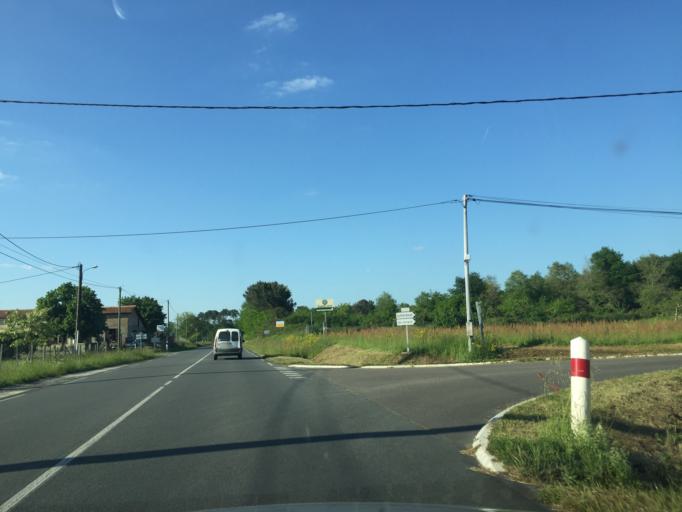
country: FR
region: Poitou-Charentes
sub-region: Departement de la Charente-Maritime
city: Saint-Aigulin
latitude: 45.1383
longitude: -0.0028
